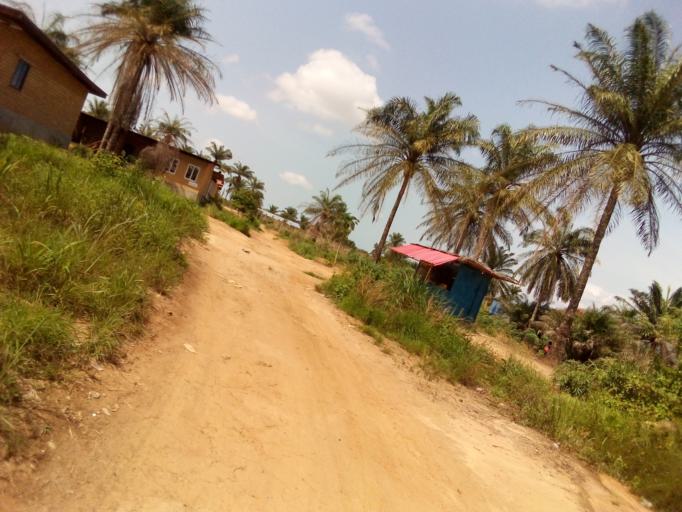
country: SL
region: Western Area
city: Waterloo
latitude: 8.3468
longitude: -13.0163
